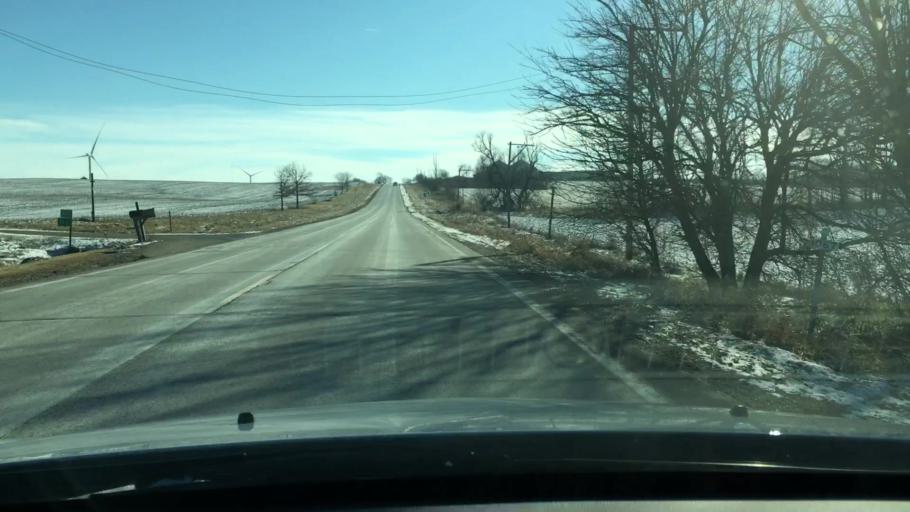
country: US
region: Illinois
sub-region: LaSalle County
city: Mendota
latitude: 41.7244
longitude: -89.0838
